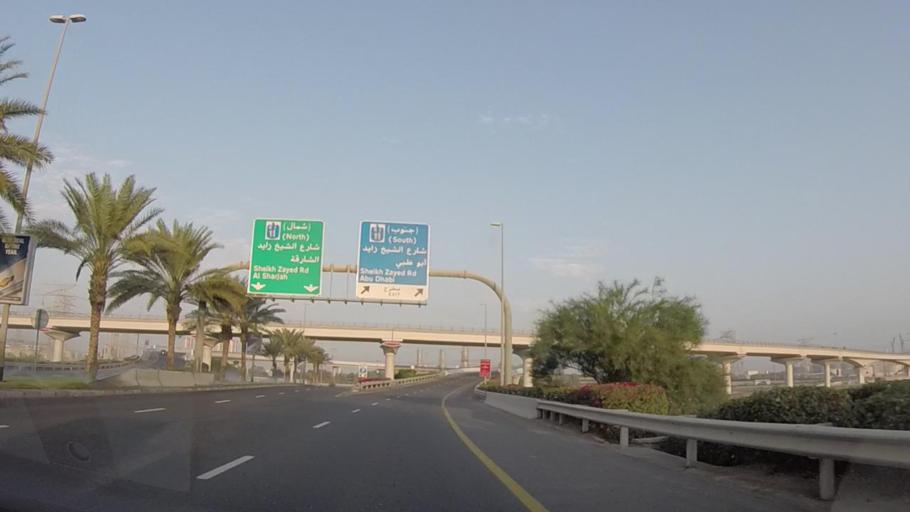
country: AE
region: Dubai
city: Dubai
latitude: 25.0527
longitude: 55.1252
